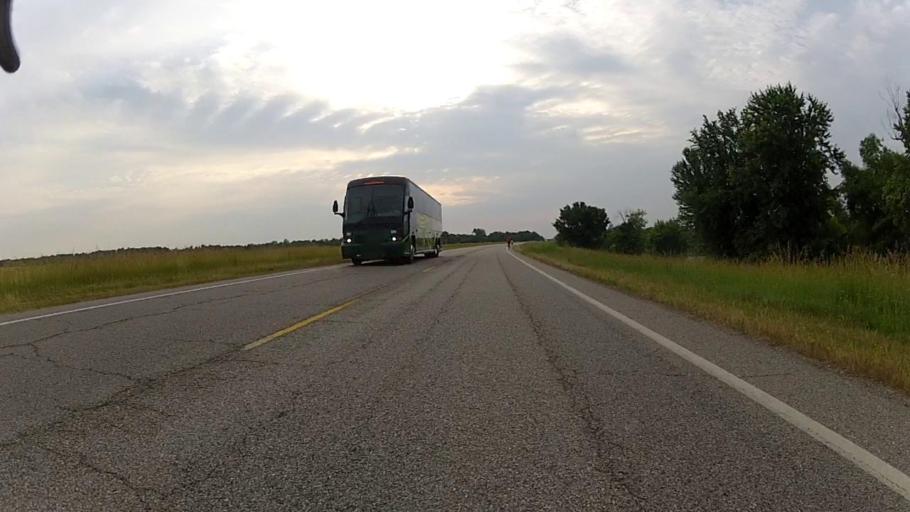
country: US
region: Kansas
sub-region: Labette County
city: Oswego
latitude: 37.1800
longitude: -94.9815
